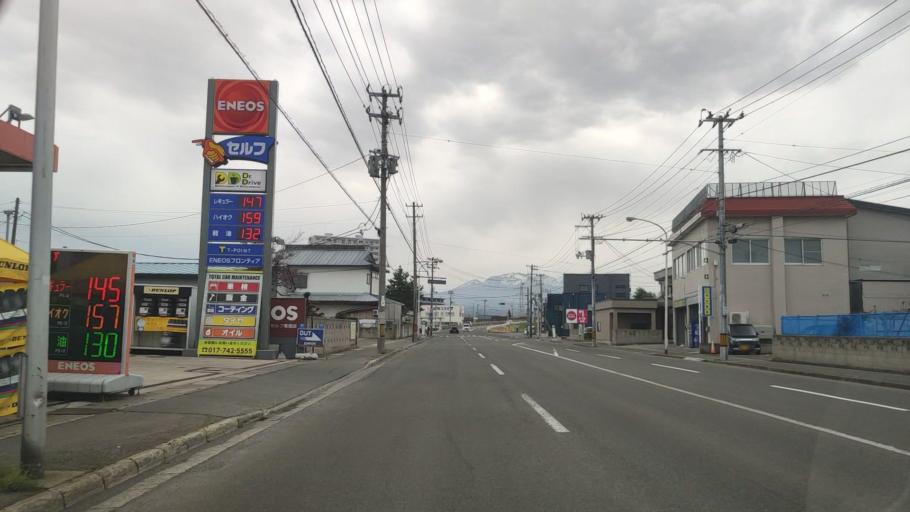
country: JP
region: Aomori
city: Aomori Shi
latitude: 40.8121
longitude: 140.7776
